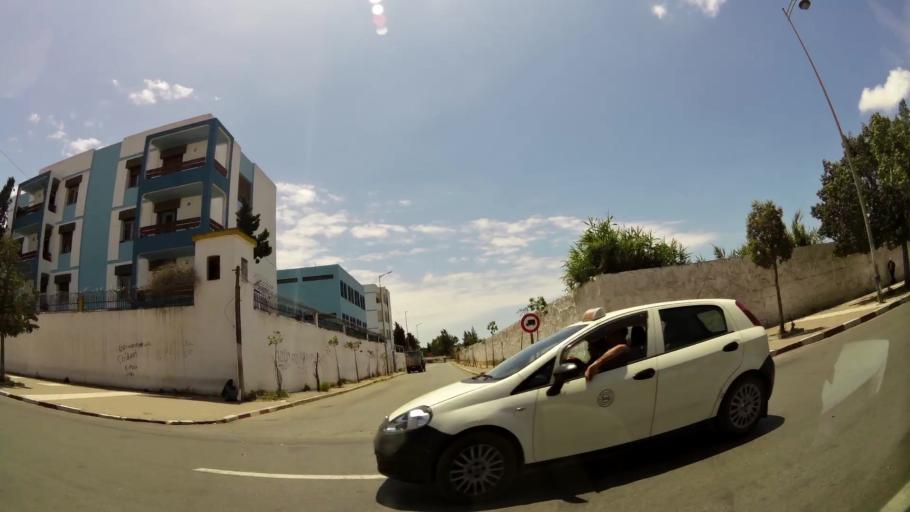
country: MA
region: Gharb-Chrarda-Beni Hssen
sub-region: Kenitra Province
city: Kenitra
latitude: 34.2511
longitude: -6.5570
